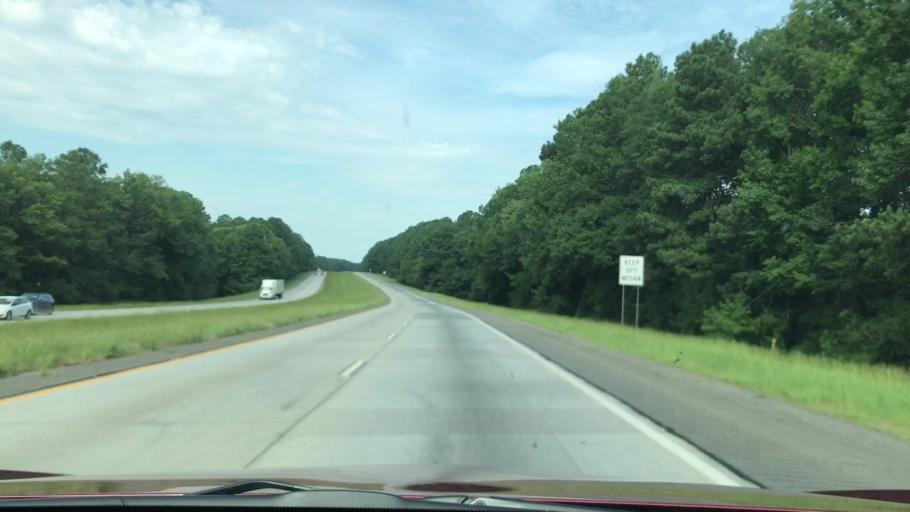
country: US
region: Georgia
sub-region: Warren County
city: Firing Range
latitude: 33.5036
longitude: -82.7688
